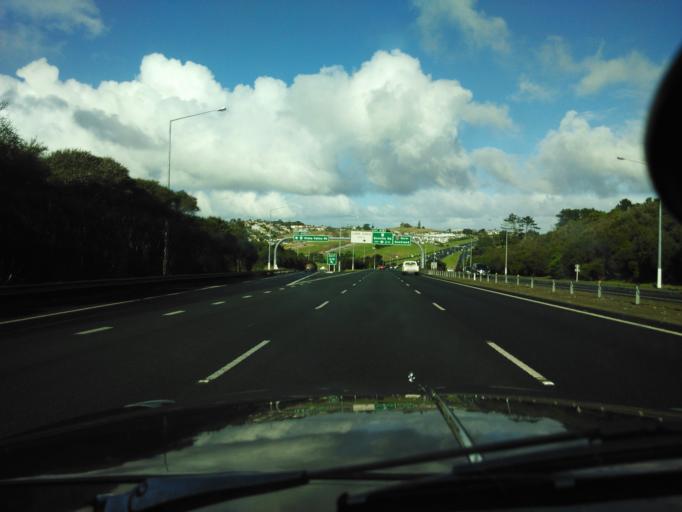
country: NZ
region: Auckland
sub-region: Auckland
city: Rothesay Bay
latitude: -36.7140
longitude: 174.7096
